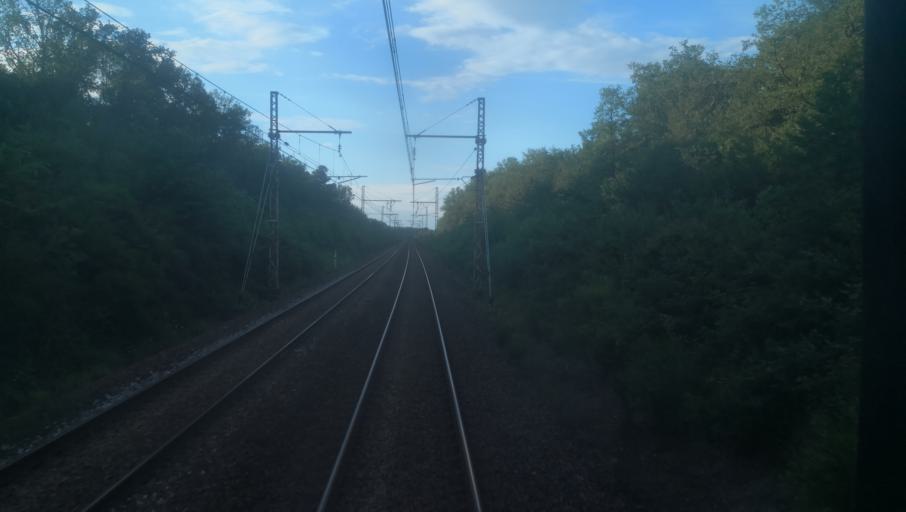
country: FR
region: Centre
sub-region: Departement de l'Indre
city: Luant
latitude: 46.7431
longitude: 1.5936
